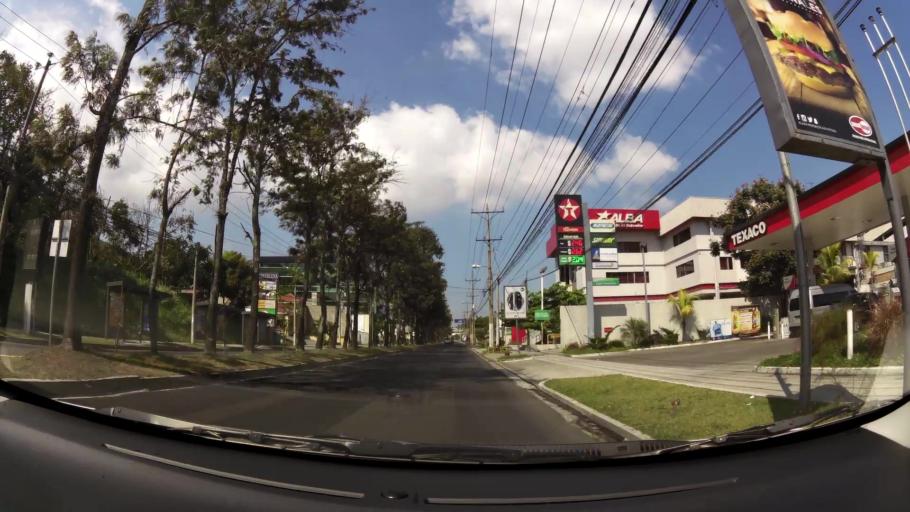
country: SV
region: La Libertad
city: Antiguo Cuscatlan
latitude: 13.6657
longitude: -89.2643
